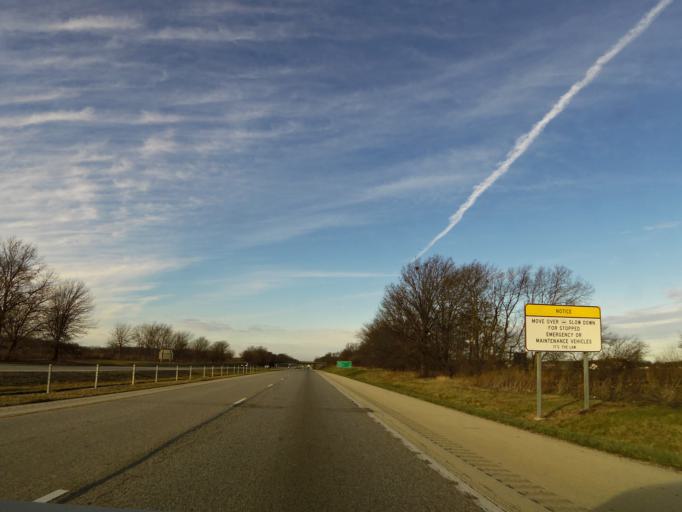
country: US
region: Illinois
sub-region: Vermilion County
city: Danville
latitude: 40.1157
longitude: -87.5534
